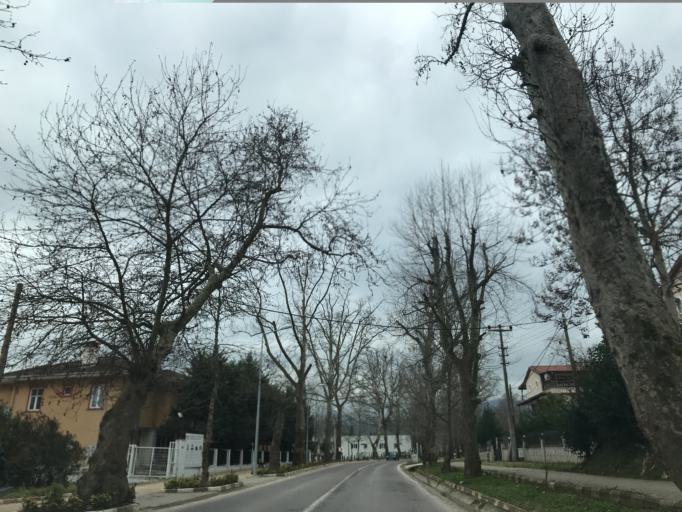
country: TR
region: Yalova
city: Kadikoy
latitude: 40.6306
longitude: 29.2236
